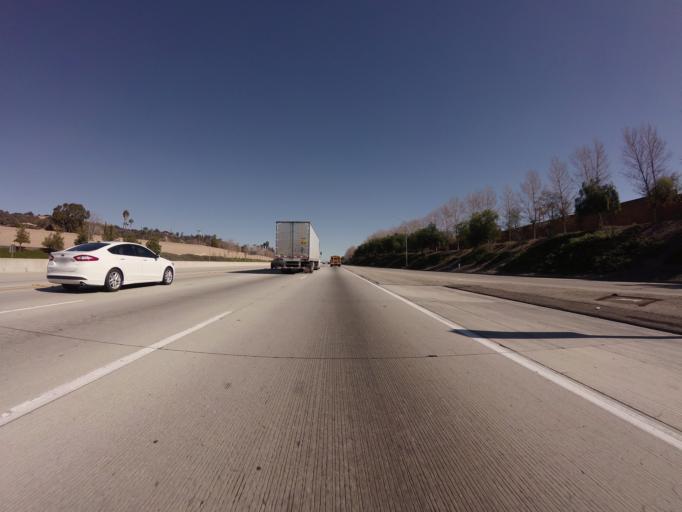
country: US
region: California
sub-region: Los Angeles County
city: Claremont
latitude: 34.1249
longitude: -117.6916
